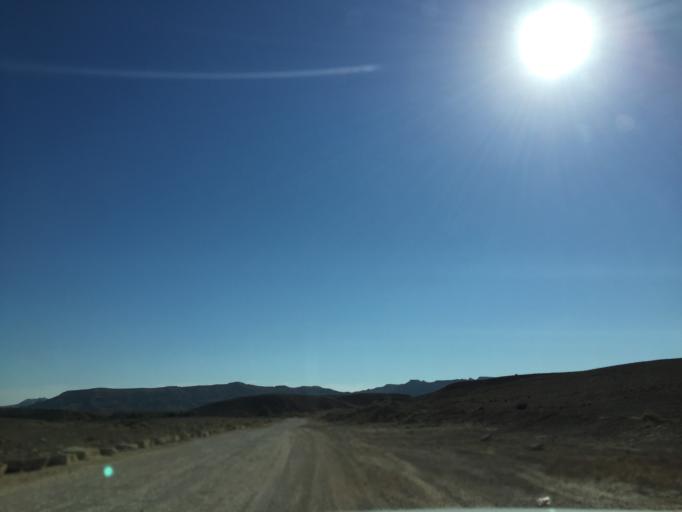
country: IL
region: Southern District
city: Mitzpe Ramon
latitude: 30.6239
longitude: 34.9211
